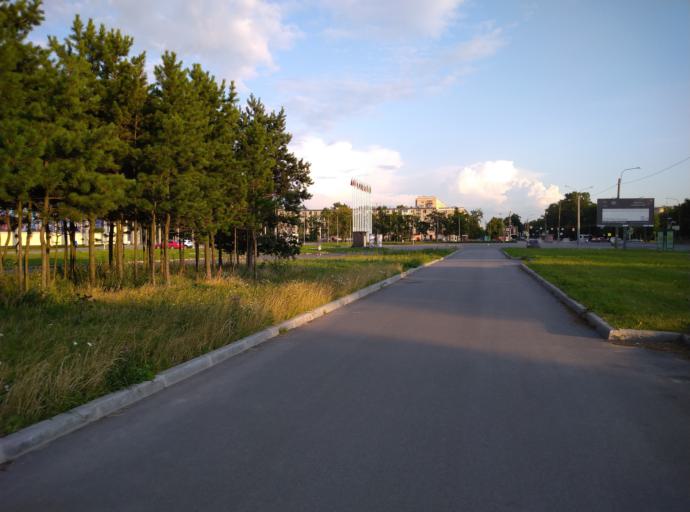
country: RU
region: St.-Petersburg
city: Kupchino
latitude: 59.8664
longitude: 30.3374
